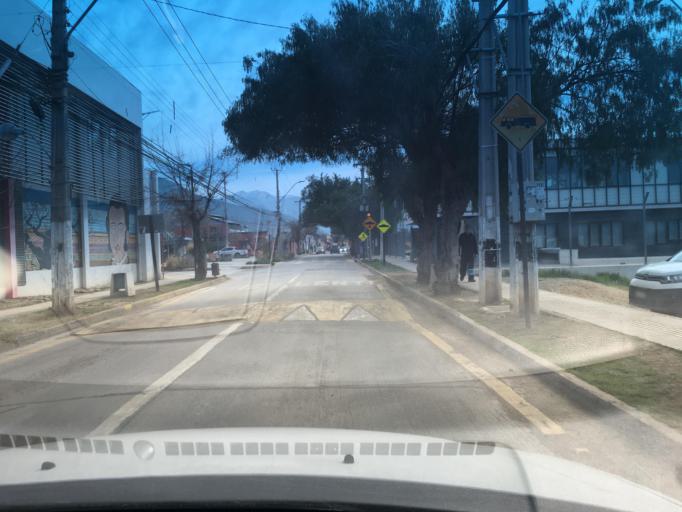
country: CL
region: Santiago Metropolitan
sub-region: Provincia de Chacabuco
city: Lampa
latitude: -33.0859
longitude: -70.9291
